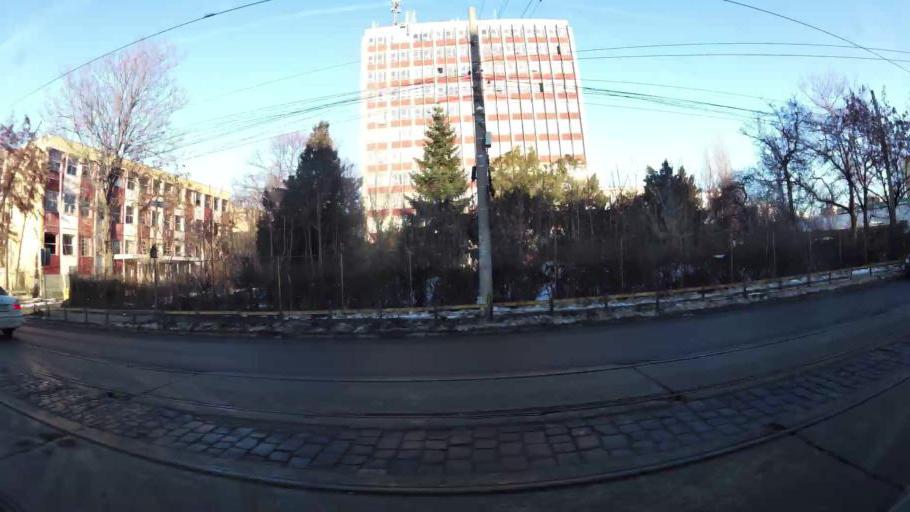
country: RO
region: Bucuresti
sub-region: Municipiul Bucuresti
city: Bucharest
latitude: 44.4484
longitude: 26.1319
